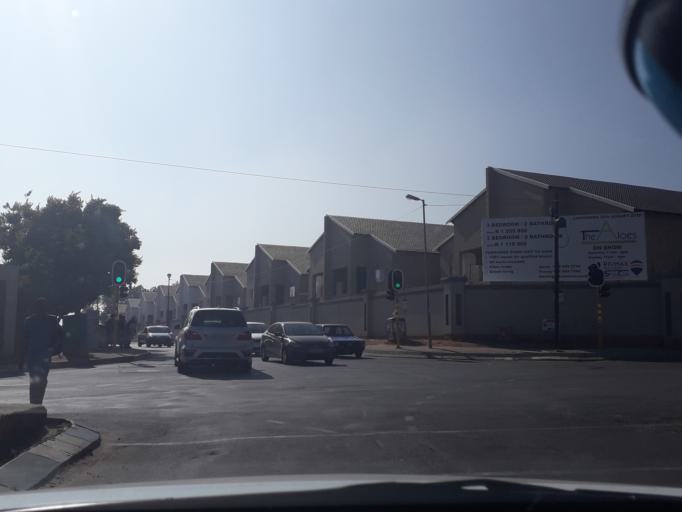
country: ZA
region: Gauteng
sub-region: City of Johannesburg Metropolitan Municipality
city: Diepsloot
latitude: -26.0460
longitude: 27.9695
